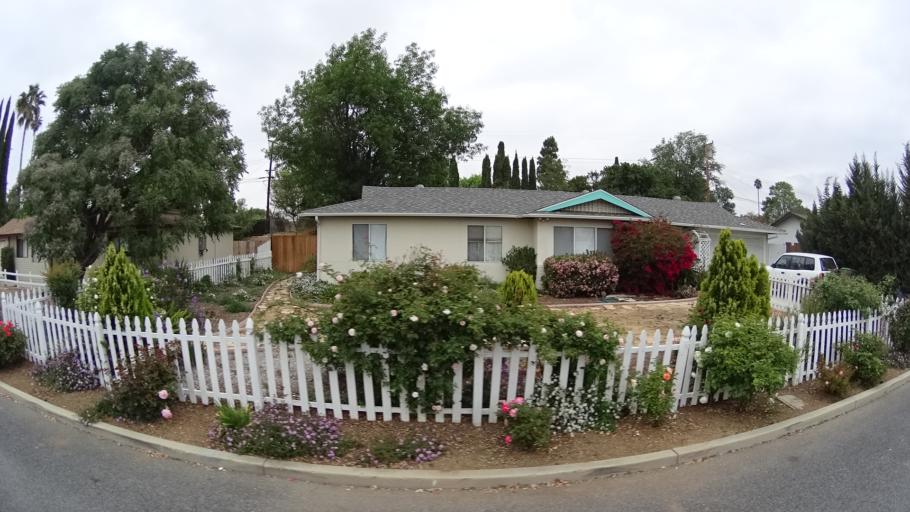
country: US
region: California
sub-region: Ventura County
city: Thousand Oaks
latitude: 34.2078
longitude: -118.8645
